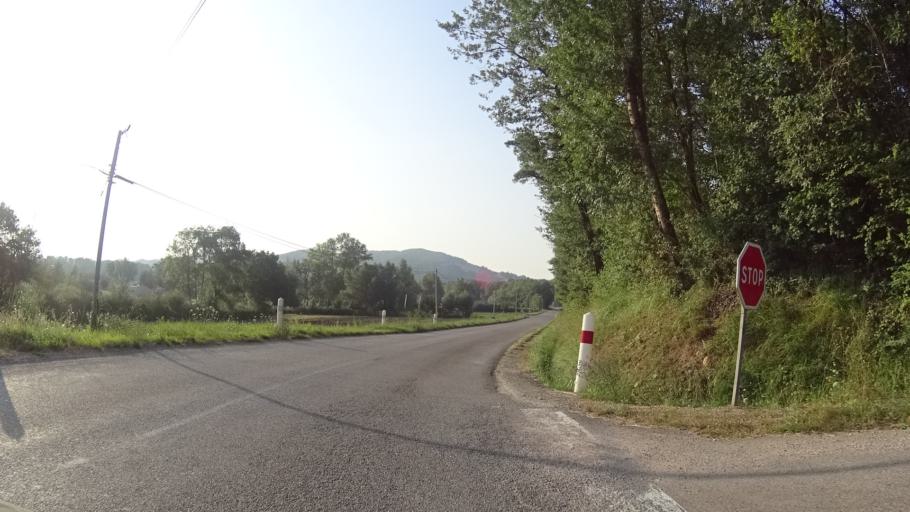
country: FR
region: Midi-Pyrenees
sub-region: Departement de l'Ariege
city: Mirepoix
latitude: 43.0800
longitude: 1.9348
